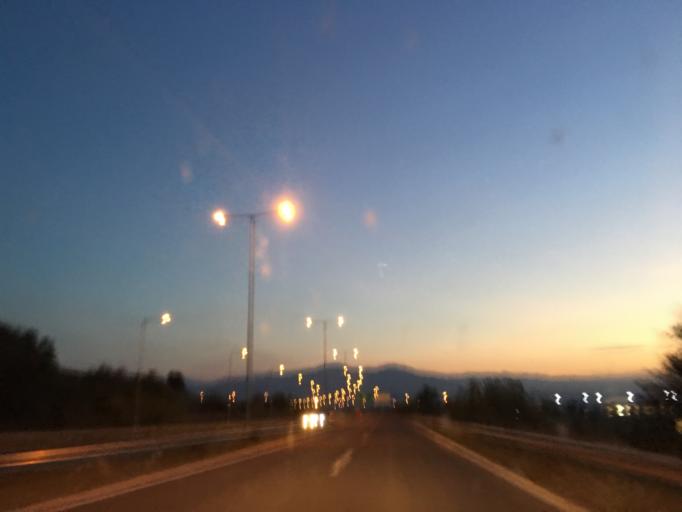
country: MK
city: Miladinovci
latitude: 41.9635
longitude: 21.6366
